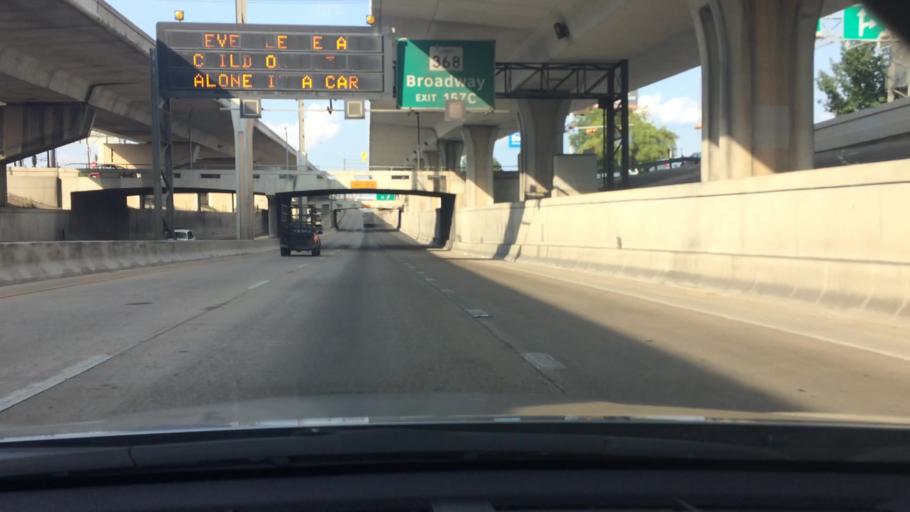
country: US
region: Texas
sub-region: Bexar County
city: San Antonio
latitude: 29.4370
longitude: -98.4911
